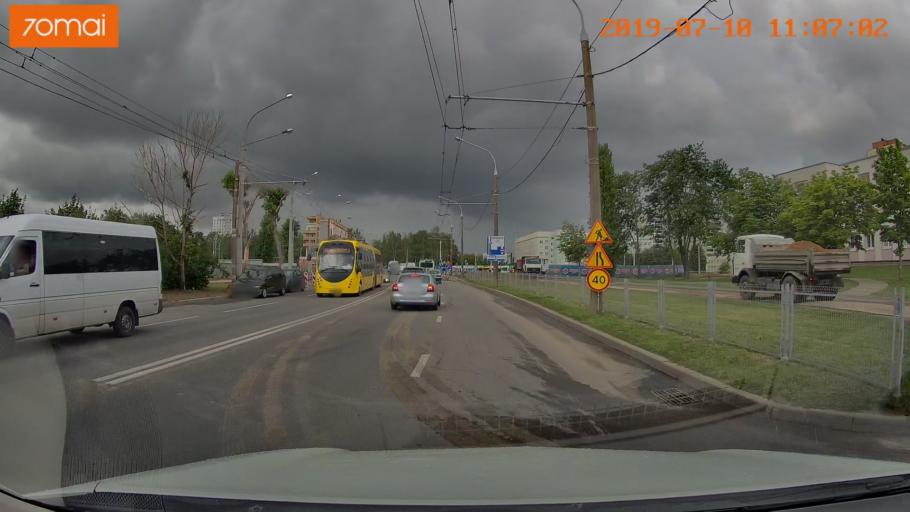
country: BY
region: Minsk
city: Syenitsa
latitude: 53.8498
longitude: 27.5392
